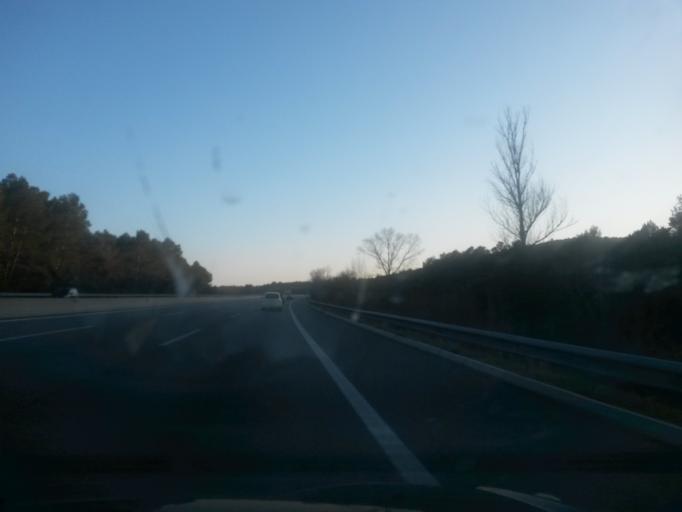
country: ES
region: Catalonia
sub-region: Provincia de Girona
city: Bascara
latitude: 42.1442
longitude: 2.9188
